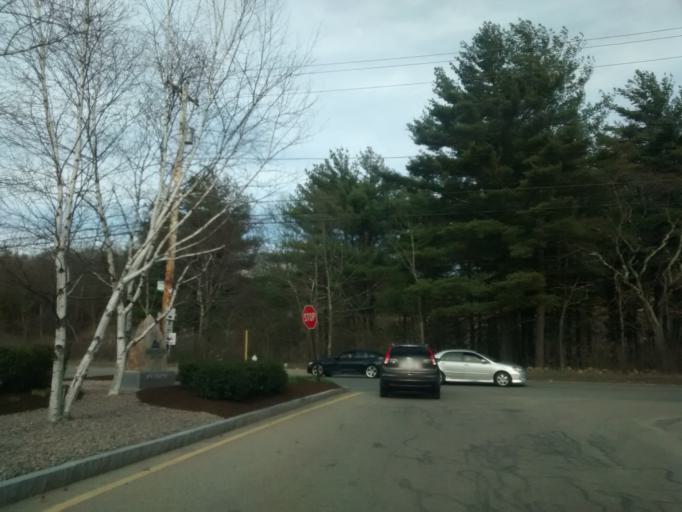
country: US
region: Massachusetts
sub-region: Norfolk County
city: Plainville
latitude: 42.0294
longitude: -71.3479
